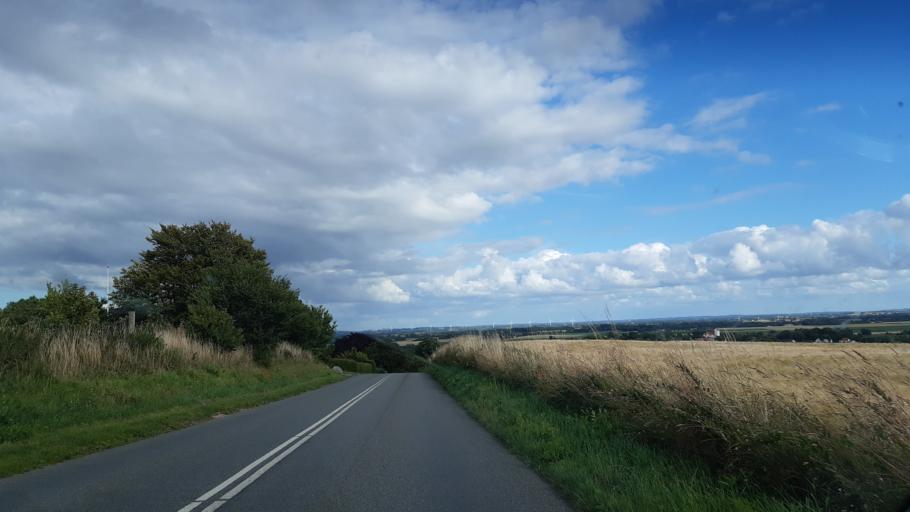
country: DK
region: Zealand
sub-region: Odsherred Kommune
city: Horve
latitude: 55.8136
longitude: 11.4269
